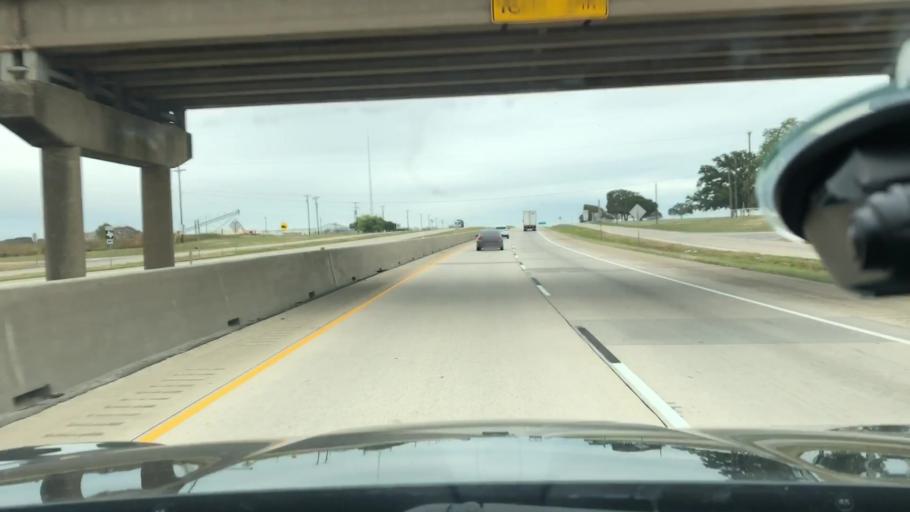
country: US
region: Texas
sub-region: Hopkins County
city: Sulphur Springs
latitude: 33.1206
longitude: -95.7090
